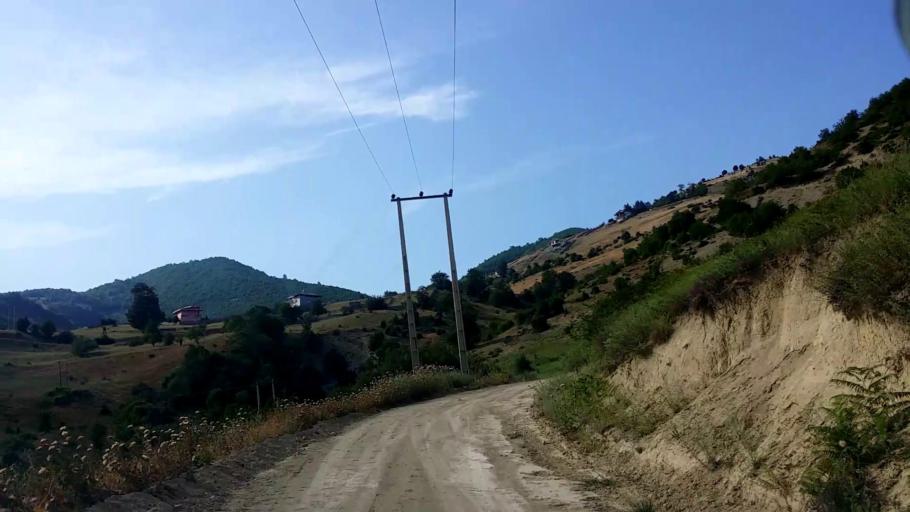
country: IR
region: Mazandaran
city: Chalus
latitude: 36.5497
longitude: 51.2944
